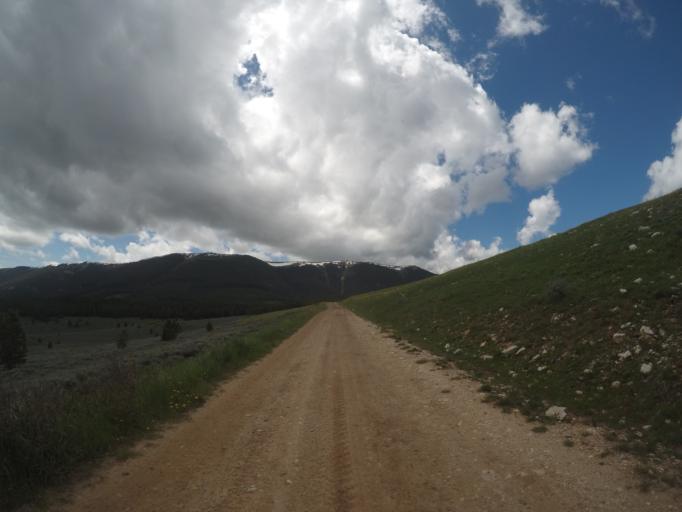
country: US
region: Wyoming
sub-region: Big Horn County
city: Lovell
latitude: 45.1796
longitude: -108.4420
